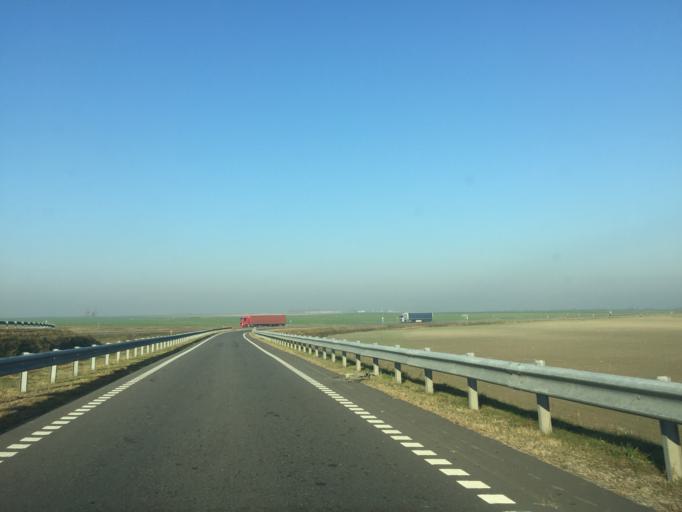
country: BY
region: Gomel
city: Kastsyukowka
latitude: 52.4908
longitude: 30.8214
